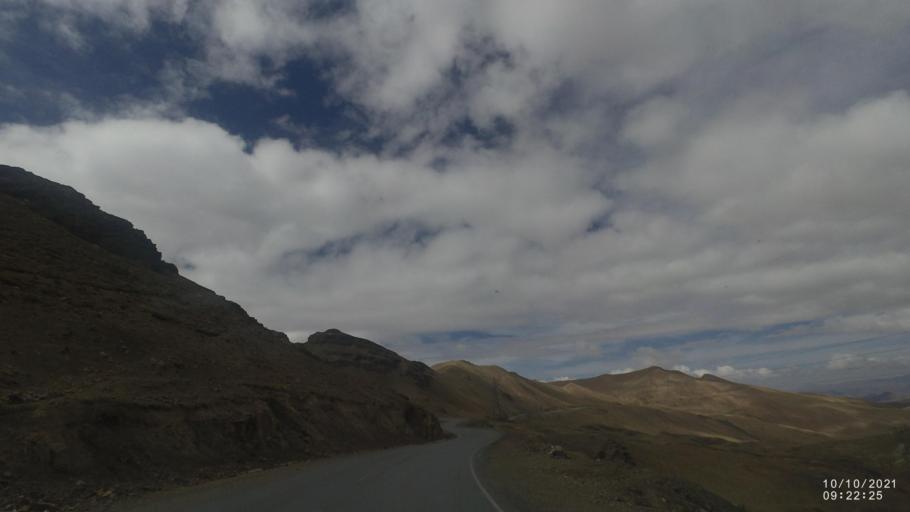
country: BO
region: La Paz
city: Quime
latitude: -17.0768
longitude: -67.2989
